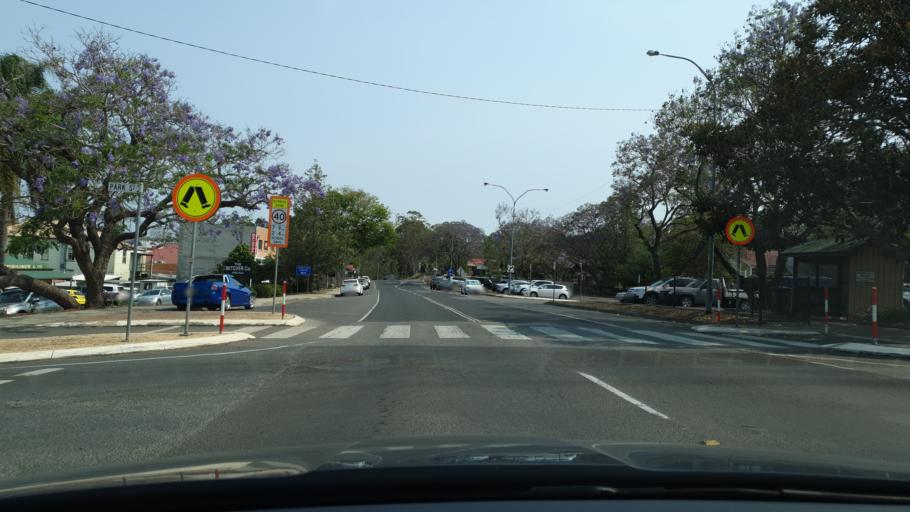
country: AU
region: Queensland
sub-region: Ipswich
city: Deebing Heights
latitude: -27.9971
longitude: 152.6815
